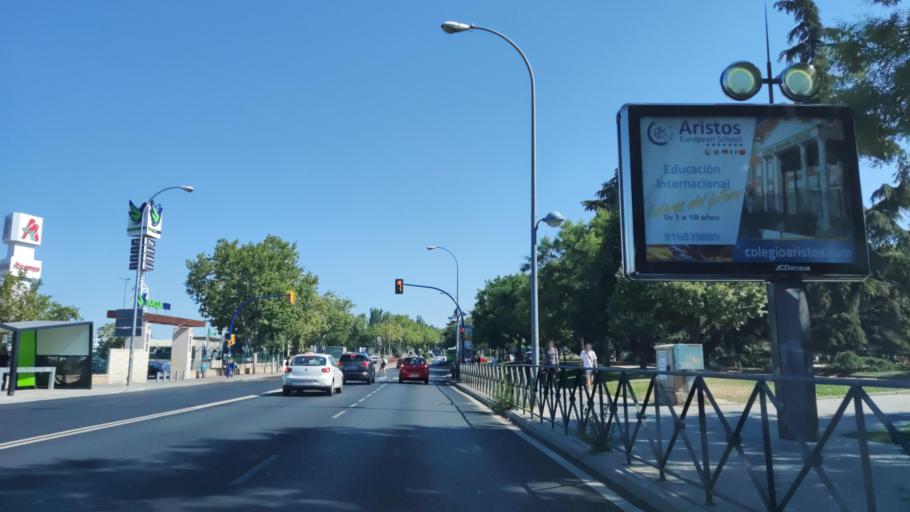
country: ES
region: Madrid
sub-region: Provincia de Madrid
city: Leganes
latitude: 40.3389
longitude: -3.7378
